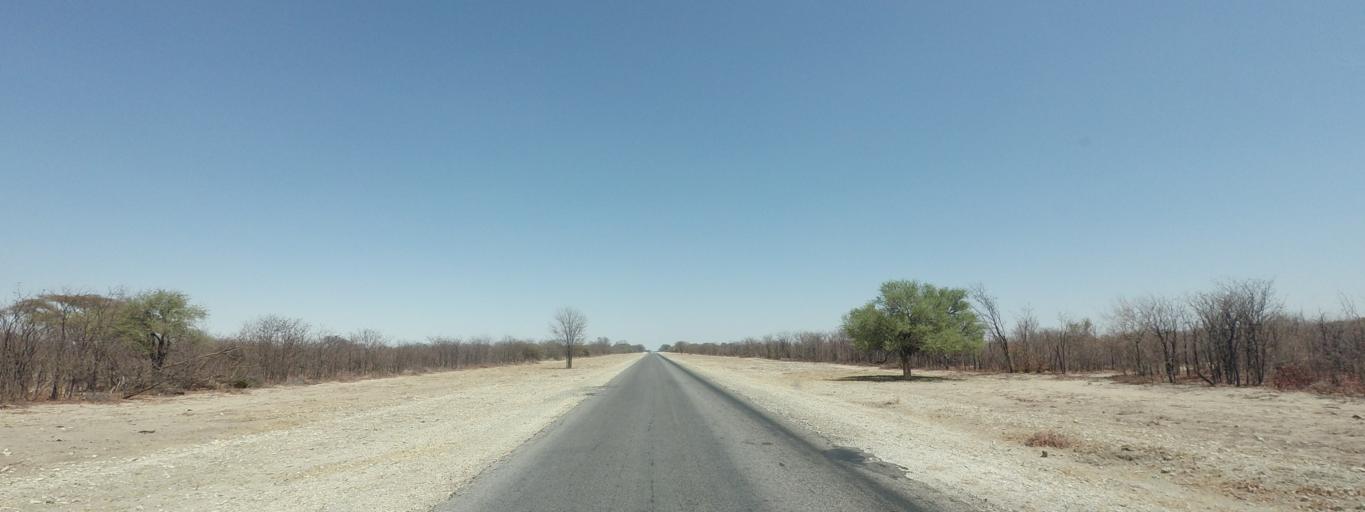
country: BW
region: North East
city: Dukwe
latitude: -20.3918
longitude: 26.3473
